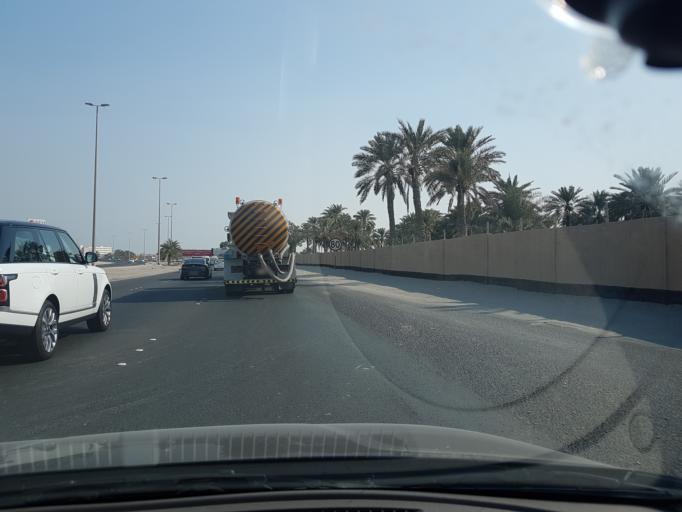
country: BH
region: Northern
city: Sitrah
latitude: 26.1621
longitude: 50.6046
